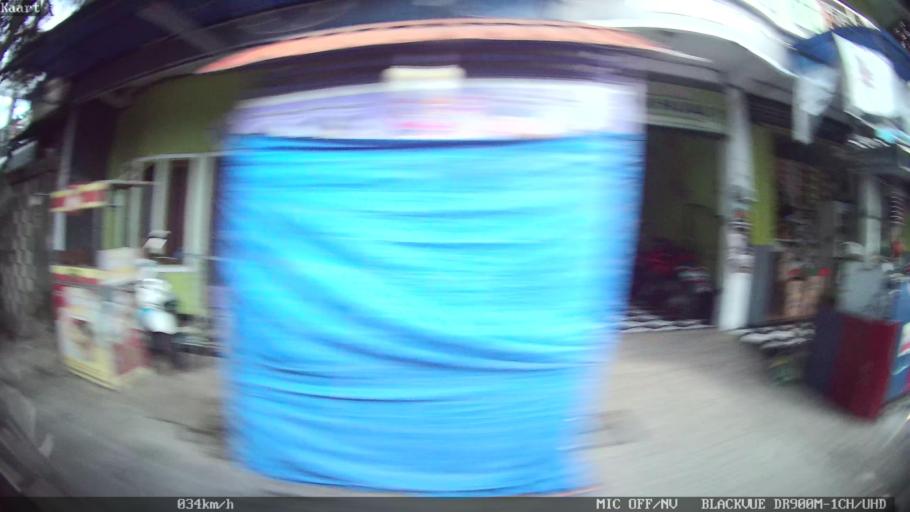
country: ID
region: Bali
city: Karyadharma
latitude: -8.7010
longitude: 115.1940
